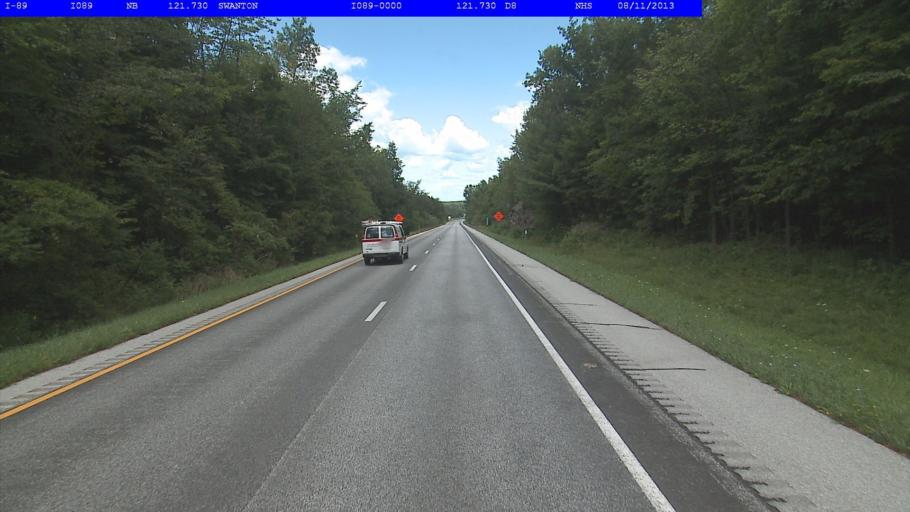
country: US
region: Vermont
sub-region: Franklin County
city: Swanton
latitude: 44.9006
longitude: -73.0938
